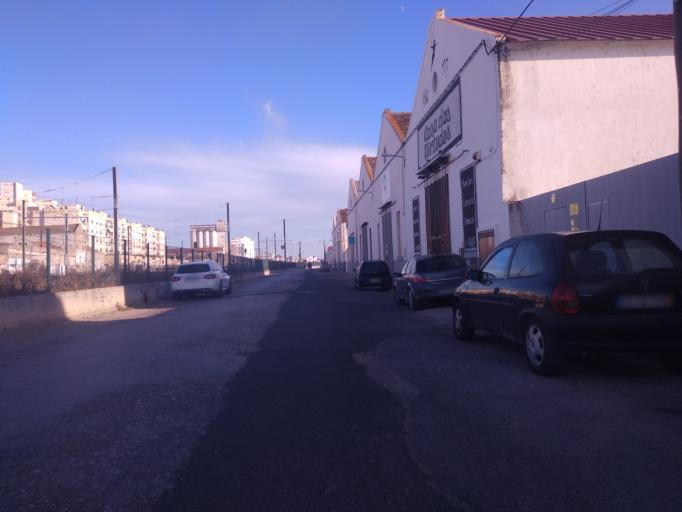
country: PT
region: Faro
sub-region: Faro
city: Faro
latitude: 37.0222
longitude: -7.9432
